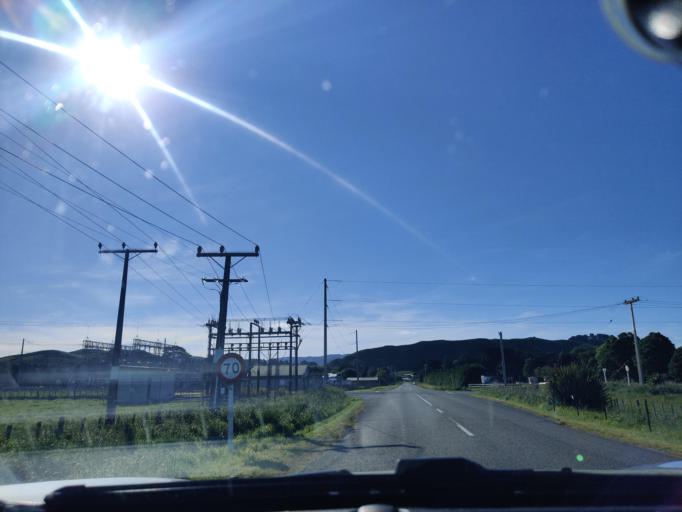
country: NZ
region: Manawatu-Wanganui
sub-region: Palmerston North City
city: Palmerston North
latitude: -40.5175
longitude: 175.7536
